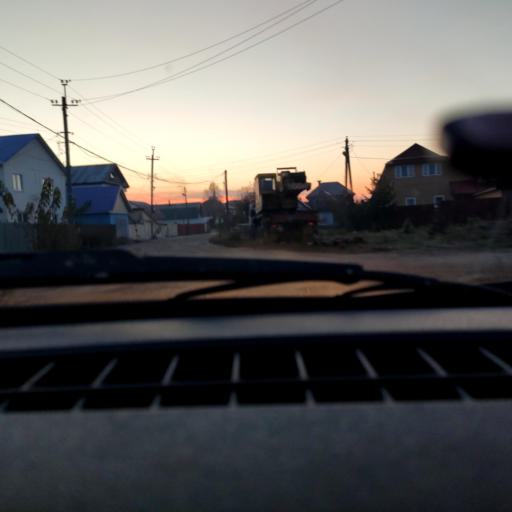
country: RU
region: Bashkortostan
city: Iglino
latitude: 54.8345
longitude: 56.1850
